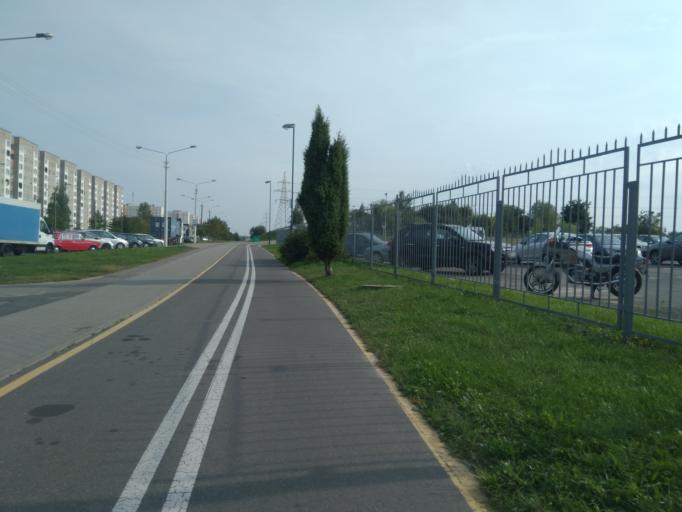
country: BY
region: Minsk
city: Minsk
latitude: 53.8618
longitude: 27.5874
